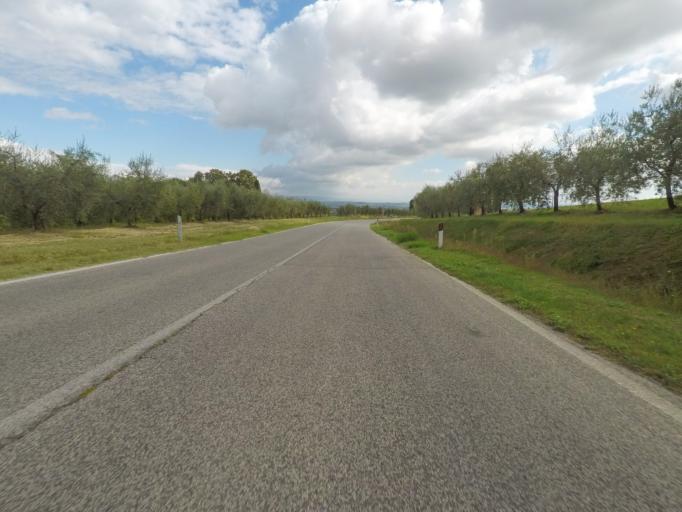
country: IT
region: Tuscany
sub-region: Provincia di Siena
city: Torrita di Siena
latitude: 43.1510
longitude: 11.7811
